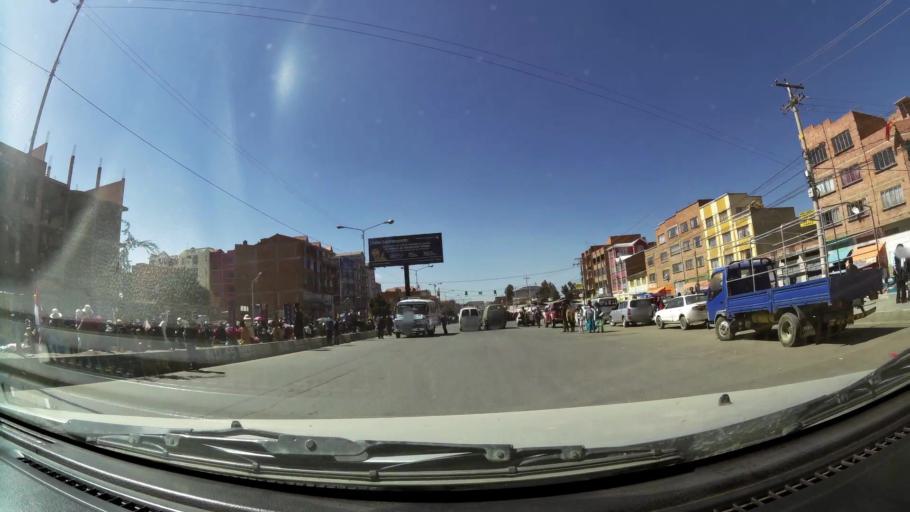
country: BO
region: La Paz
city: La Paz
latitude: -16.4982
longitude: -68.1903
